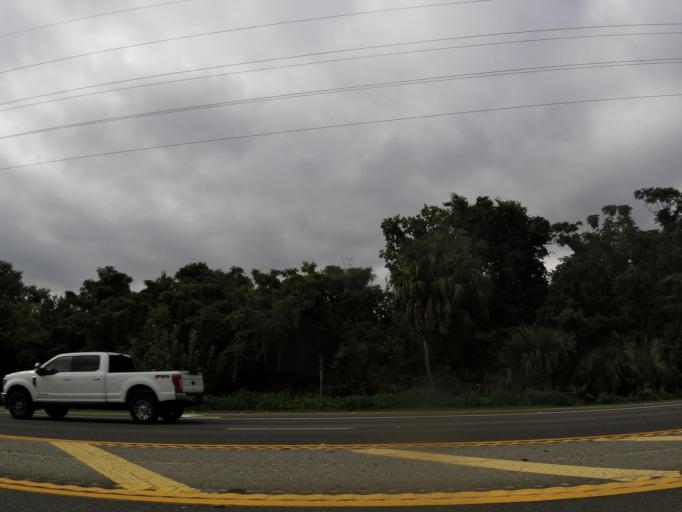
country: US
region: Georgia
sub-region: Glynn County
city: Brunswick
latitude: 31.1618
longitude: -81.4678
